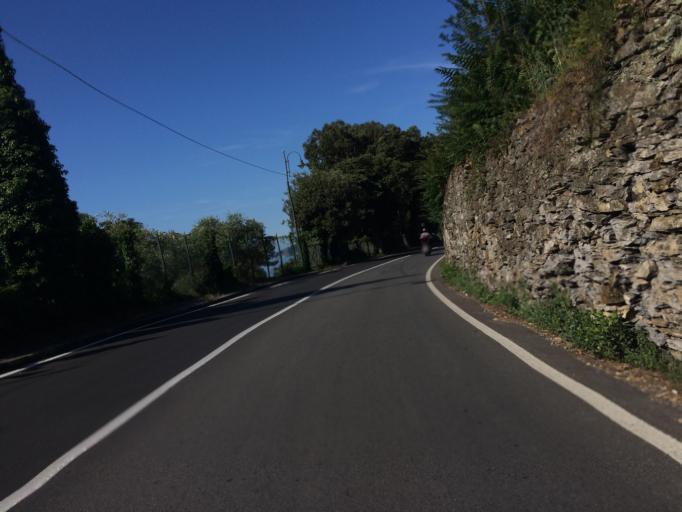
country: IT
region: Liguria
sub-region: Provincia di Genova
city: Rapallo
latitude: 44.3430
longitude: 9.2473
